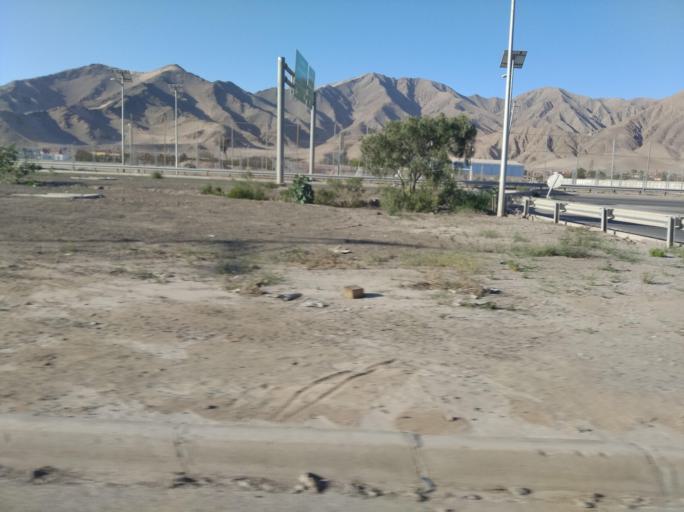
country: CL
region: Atacama
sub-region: Provincia de Copiapo
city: Copiapo
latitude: -27.3516
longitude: -70.3554
